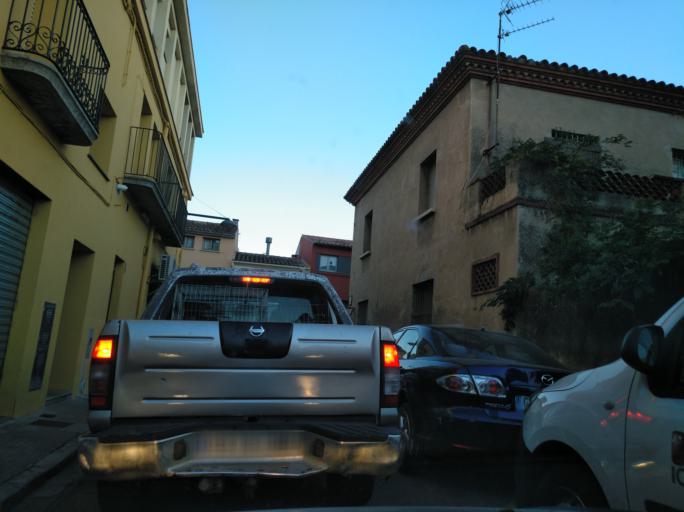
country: ES
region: Catalonia
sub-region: Provincia de Girona
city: Salt
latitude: 41.9734
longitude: 2.7836
